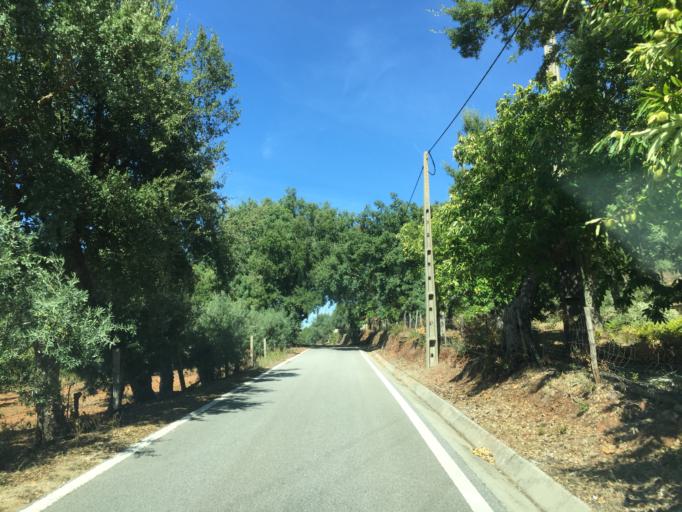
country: PT
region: Portalegre
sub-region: Marvao
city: Marvao
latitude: 39.3721
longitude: -7.3814
